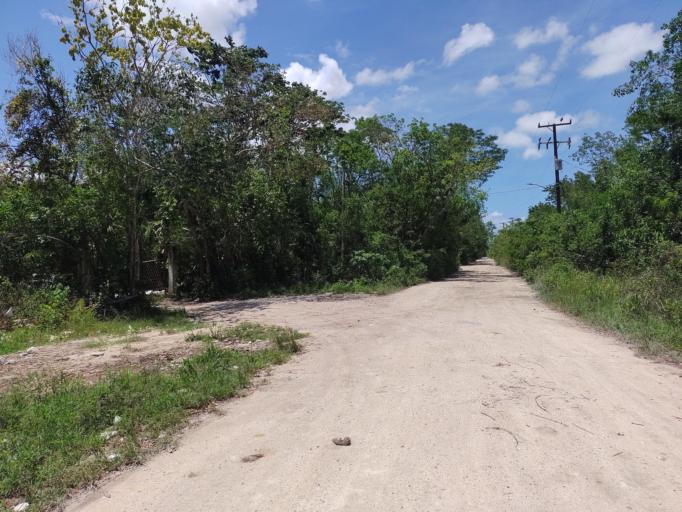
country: MX
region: Quintana Roo
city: San Miguel de Cozumel
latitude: 20.4919
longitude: -86.9064
